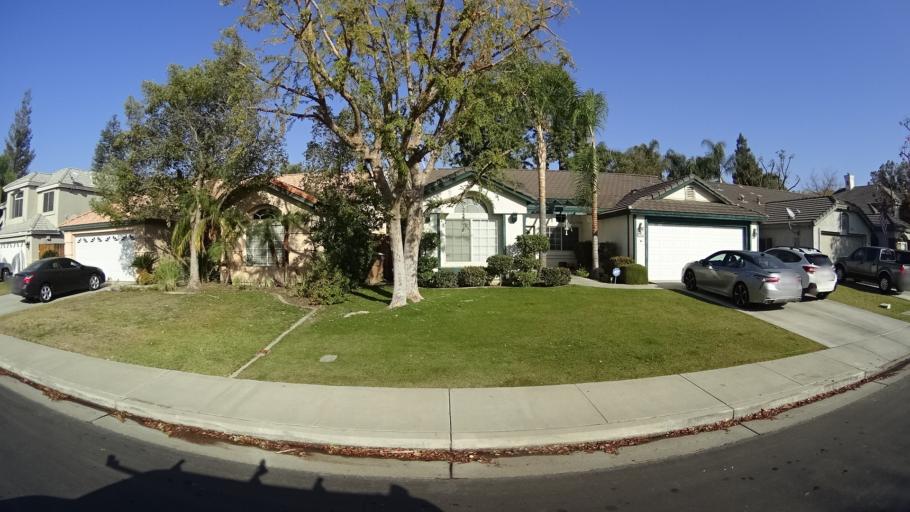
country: US
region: California
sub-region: Kern County
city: Greenacres
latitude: 35.3676
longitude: -119.1063
